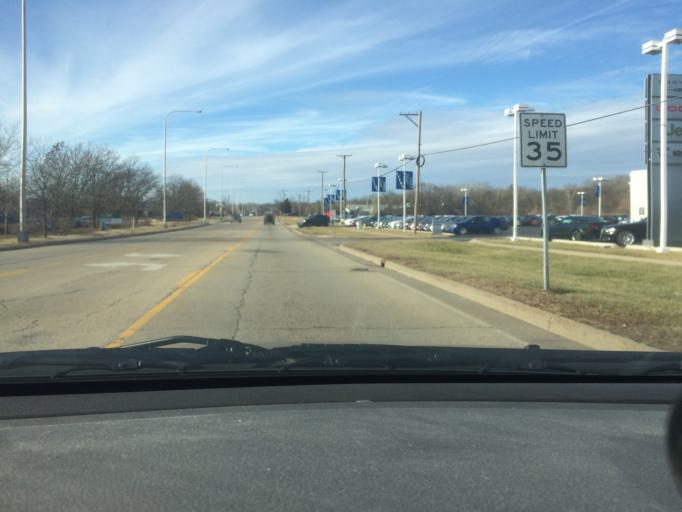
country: US
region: Illinois
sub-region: Kane County
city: Elgin
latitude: 42.0330
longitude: -88.2514
